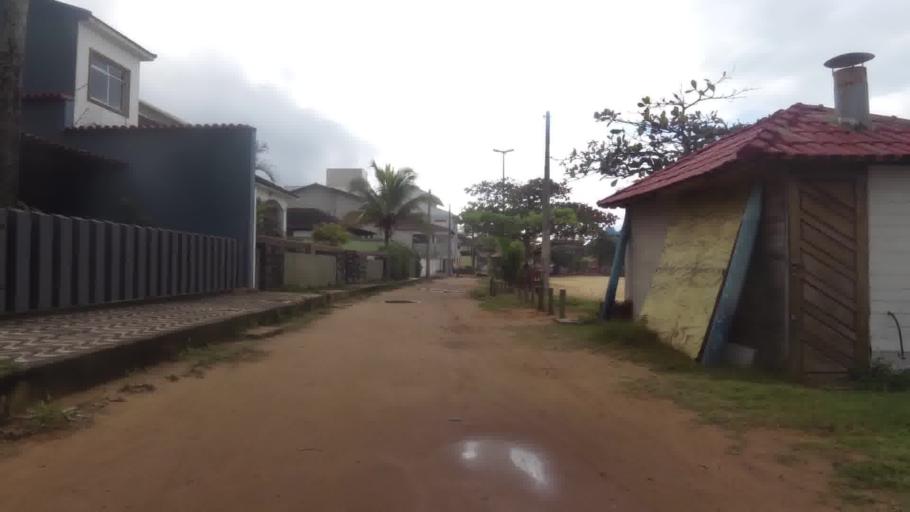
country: BR
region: Espirito Santo
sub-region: Piuma
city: Piuma
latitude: -20.8334
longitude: -40.6990
